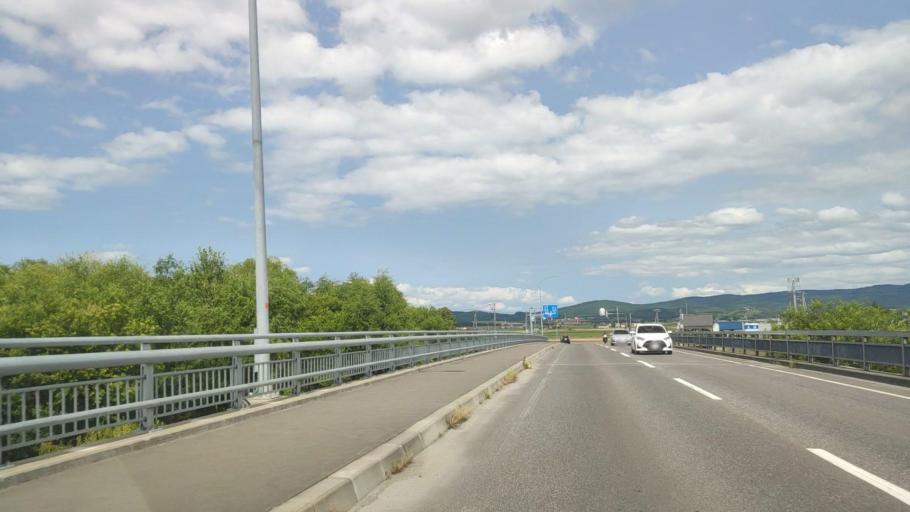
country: JP
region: Hokkaido
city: Nayoro
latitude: 44.1903
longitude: 142.4143
